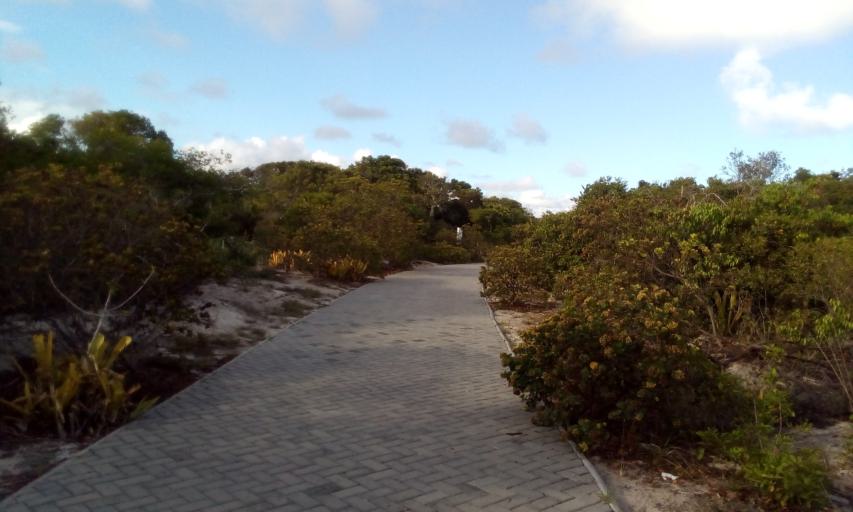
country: BR
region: Bahia
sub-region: Mata De Sao Joao
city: Mata de Sao Joao
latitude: -12.5739
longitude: -38.0092
